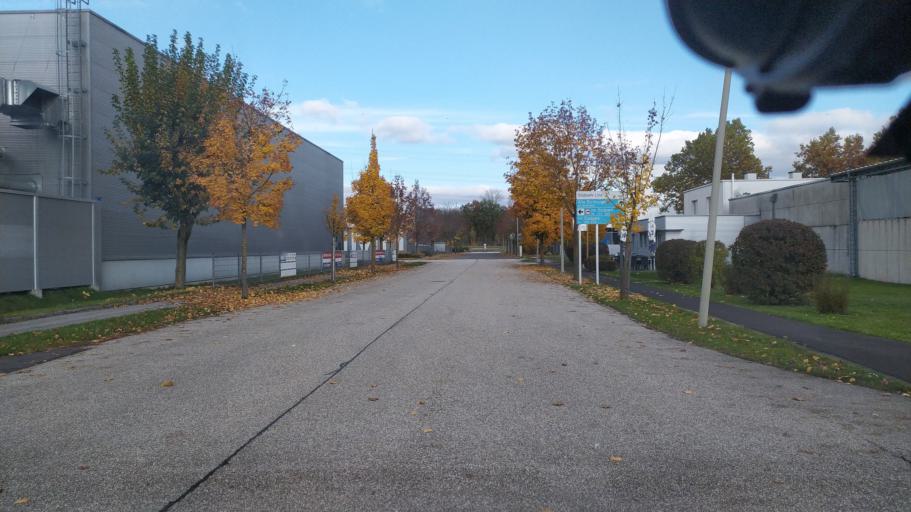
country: AT
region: Upper Austria
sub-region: Politischer Bezirk Urfahr-Umgebung
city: Steyregg
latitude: 48.2528
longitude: 14.3792
